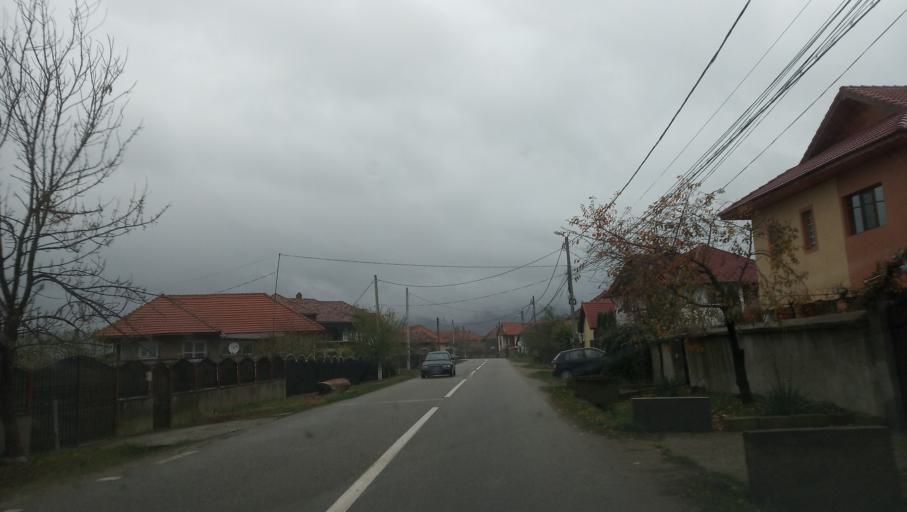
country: RO
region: Gorj
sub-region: Comuna Musetesti
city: Musetesti
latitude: 45.1405
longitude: 23.4617
